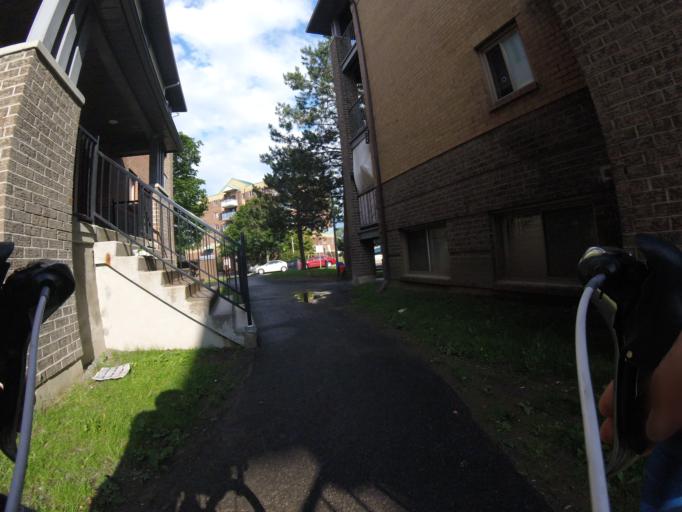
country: CA
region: Ontario
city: Ottawa
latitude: 45.4202
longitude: -75.6697
